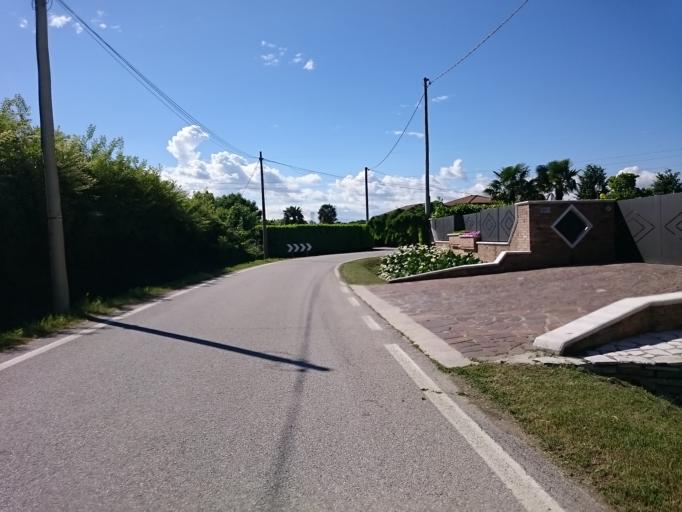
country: IT
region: Veneto
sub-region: Provincia di Padova
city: Saonara
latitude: 45.3574
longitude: 12.0013
